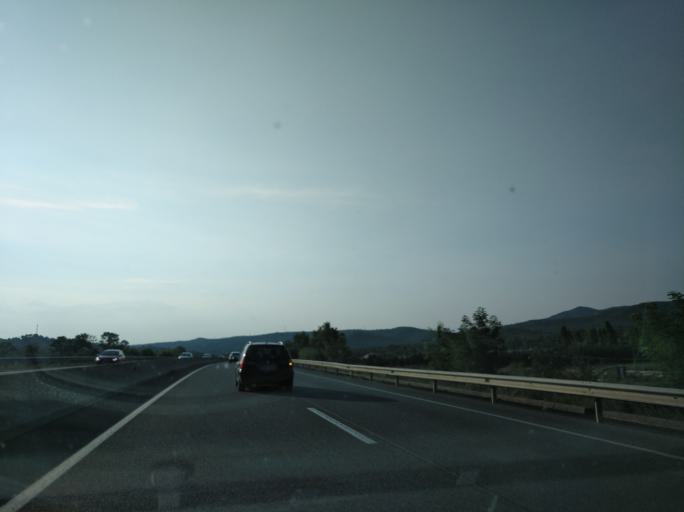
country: ES
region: Catalonia
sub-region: Provincia de Girona
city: Santa Cristina d'Aro
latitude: 41.8176
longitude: 2.9817
